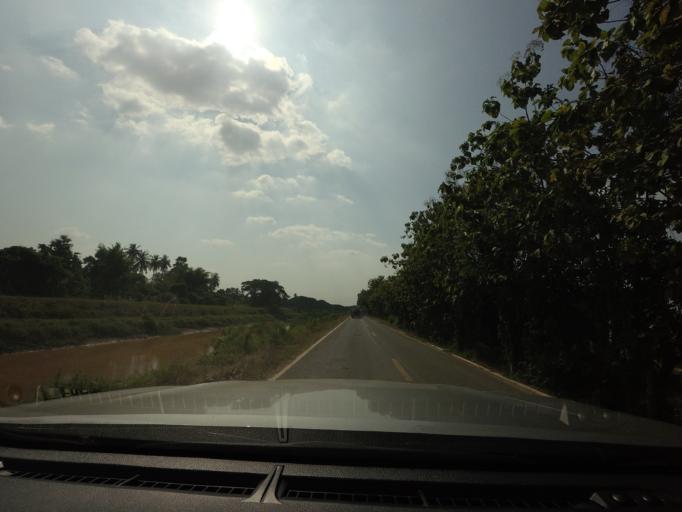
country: TH
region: Phitsanulok
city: Phitsanulok
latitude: 16.8075
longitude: 100.2181
